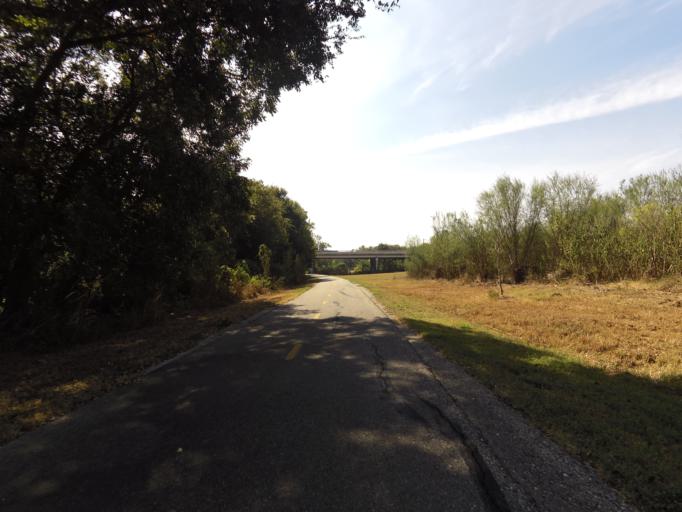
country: US
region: Texas
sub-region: Bexar County
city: Kirby
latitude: 29.4367
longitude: -98.4200
